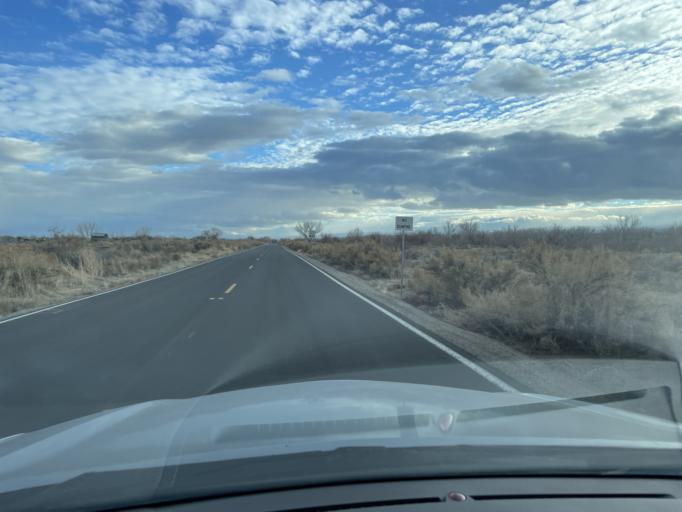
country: US
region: Colorado
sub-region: Montrose County
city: Olathe
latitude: 38.6492
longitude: -107.9953
